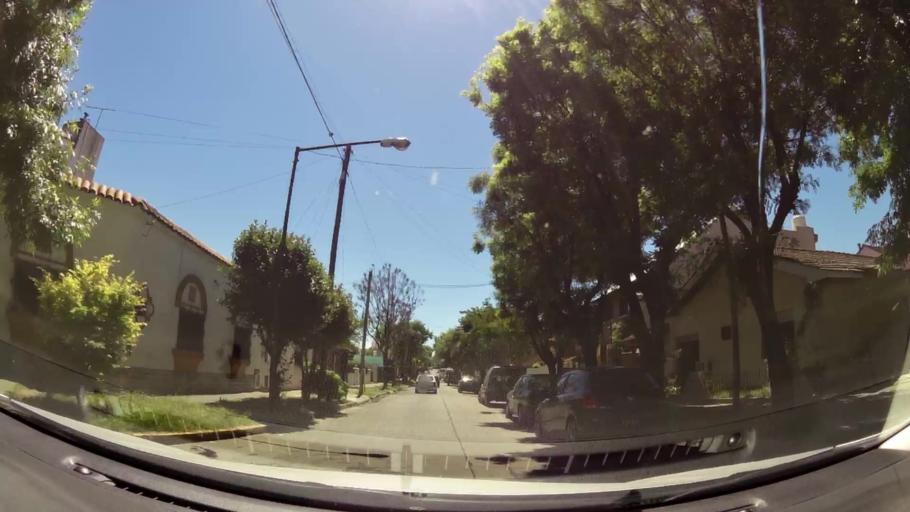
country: AR
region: Buenos Aires
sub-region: Partido de San Isidro
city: San Isidro
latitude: -34.4741
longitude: -58.5305
